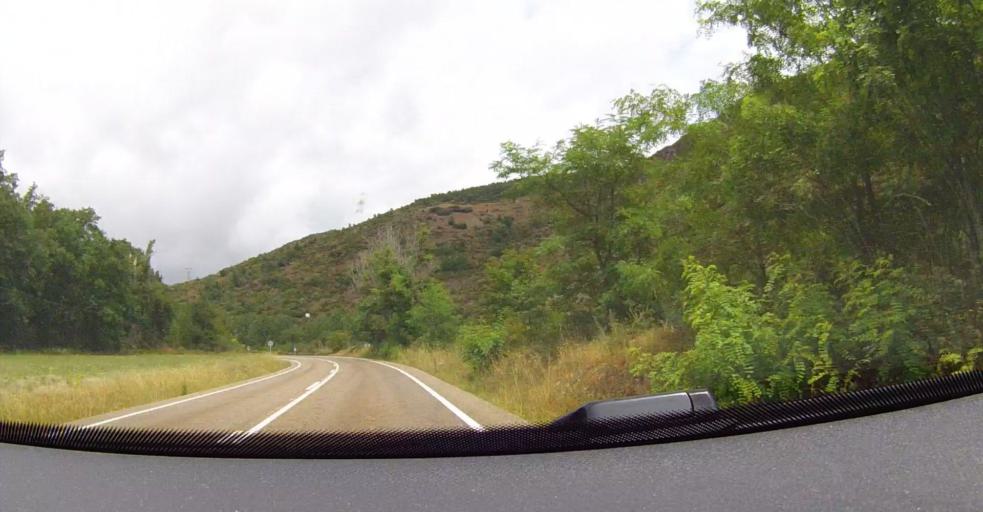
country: ES
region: Castille and Leon
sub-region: Provincia de Leon
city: Bonar
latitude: 42.8942
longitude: -5.3075
